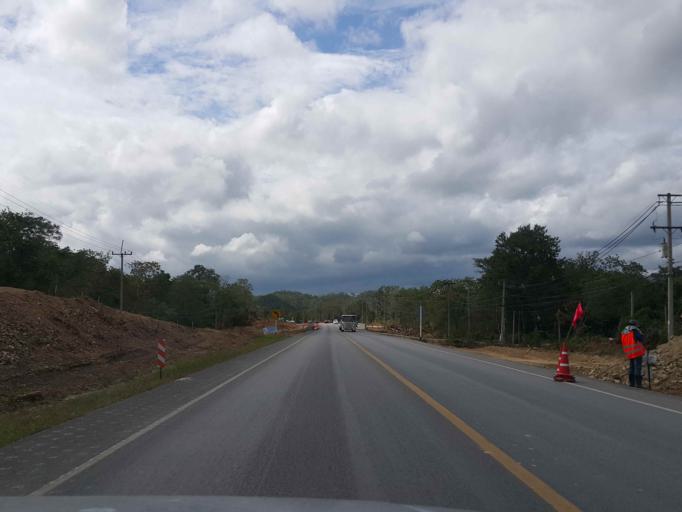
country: TH
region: Tak
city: Tak
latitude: 16.7943
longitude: 99.0114
